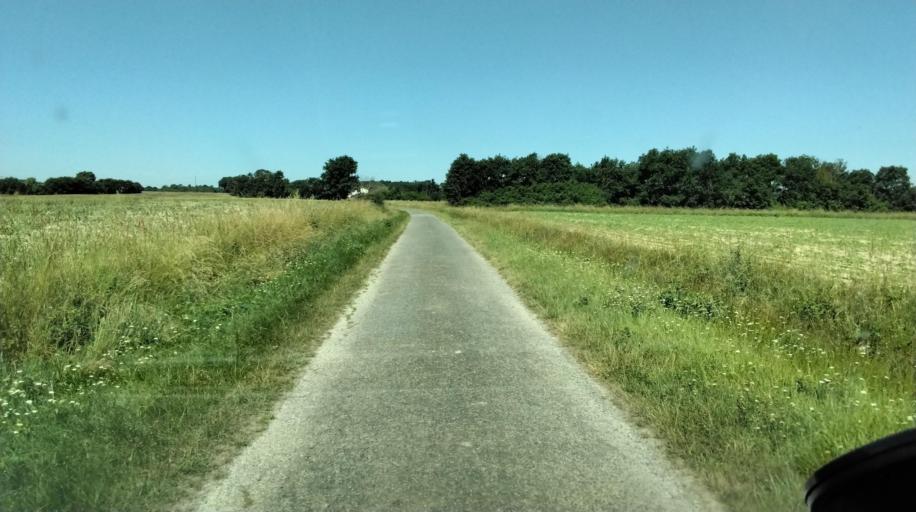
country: FR
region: Midi-Pyrenees
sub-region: Departement de la Haute-Garonne
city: Sainte-Foy-de-Peyrolieres
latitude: 43.4842
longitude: 1.1378
